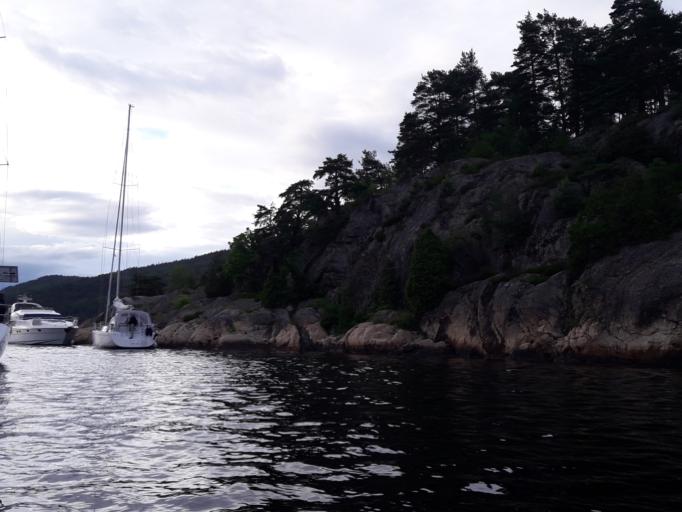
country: NO
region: Akershus
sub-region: Frogn
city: Drobak
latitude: 59.6683
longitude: 10.5787
